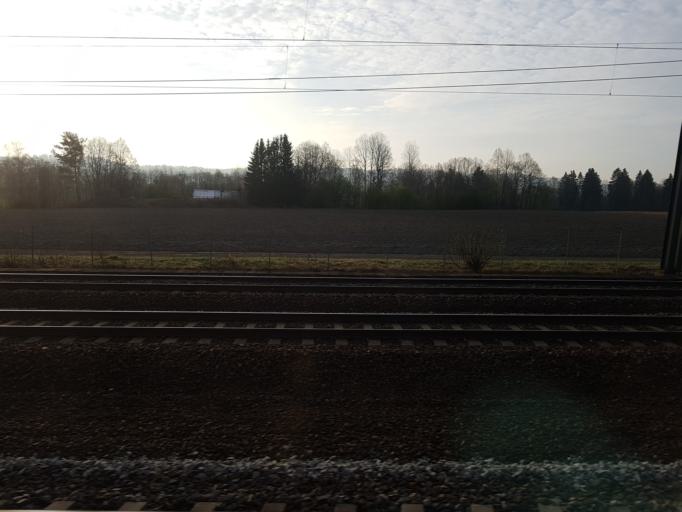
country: NO
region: Akershus
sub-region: Skedsmo
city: Leirsund
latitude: 59.9821
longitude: 11.0736
